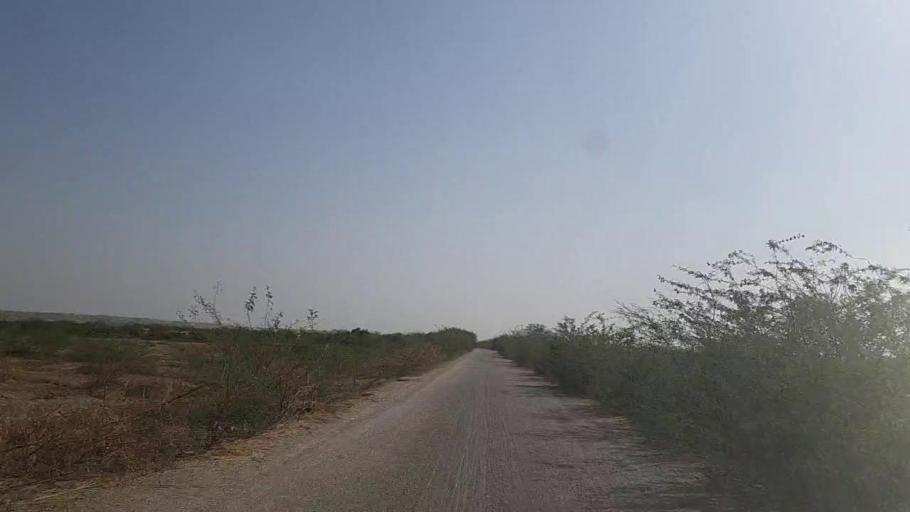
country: PK
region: Sindh
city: Kadhan
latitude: 24.5646
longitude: 69.2764
